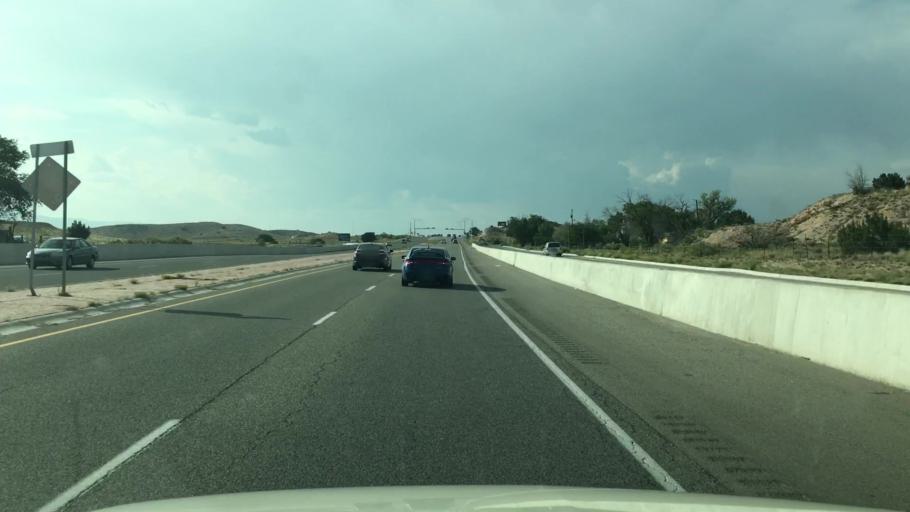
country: US
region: New Mexico
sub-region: Santa Fe County
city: El Valle de Arroyo Seco
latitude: 35.9712
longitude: -106.0398
